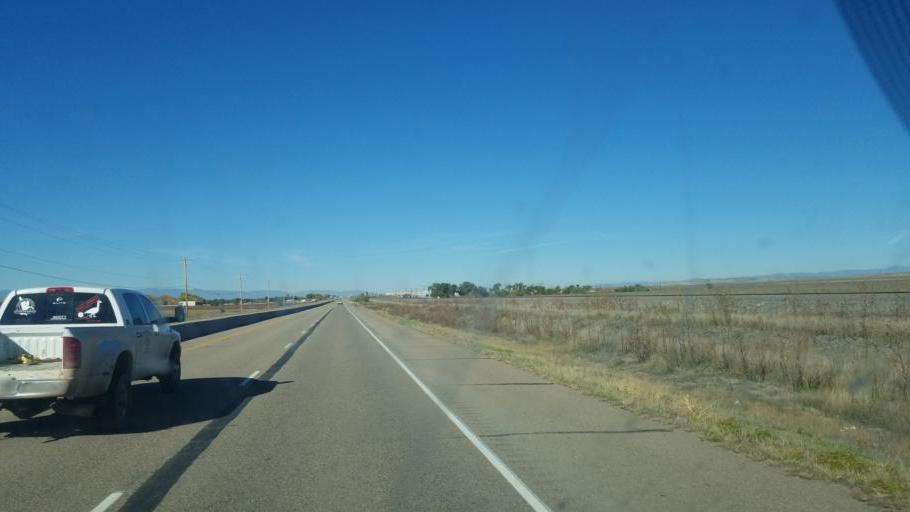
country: US
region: Colorado
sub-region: Pueblo County
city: Pueblo
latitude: 38.2727
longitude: -104.4350
